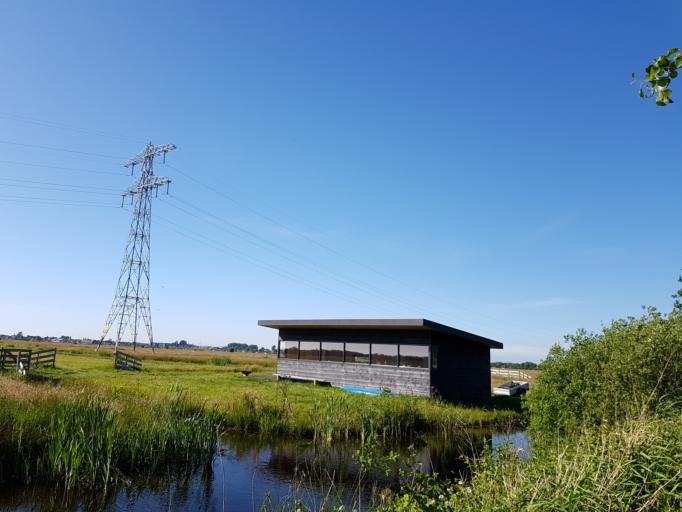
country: NL
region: South Holland
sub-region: Gemeente Gouda
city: Gouda
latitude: 51.9807
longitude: 4.7035
